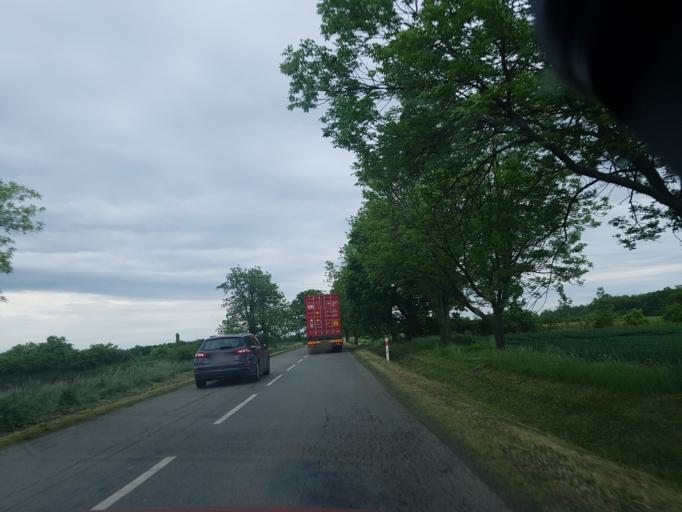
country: PL
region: Lower Silesian Voivodeship
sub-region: Powiat wroclawski
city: Kobierzyce
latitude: 50.9413
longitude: 16.9262
